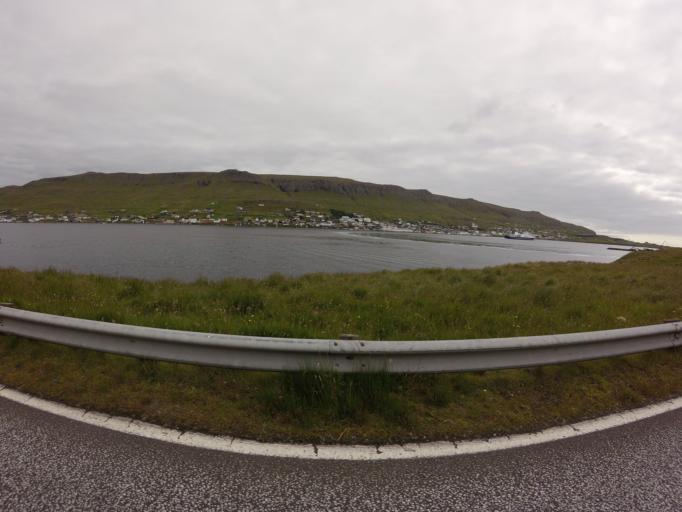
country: FO
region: Suduroy
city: Tvoroyri
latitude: 61.5506
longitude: -6.8275
